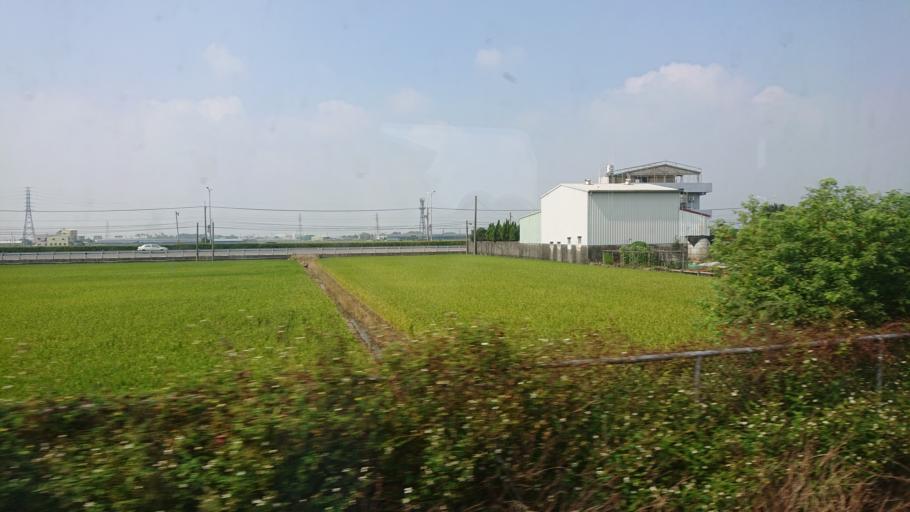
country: TW
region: Taiwan
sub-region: Yunlin
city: Douliu
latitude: 23.6468
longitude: 120.4721
